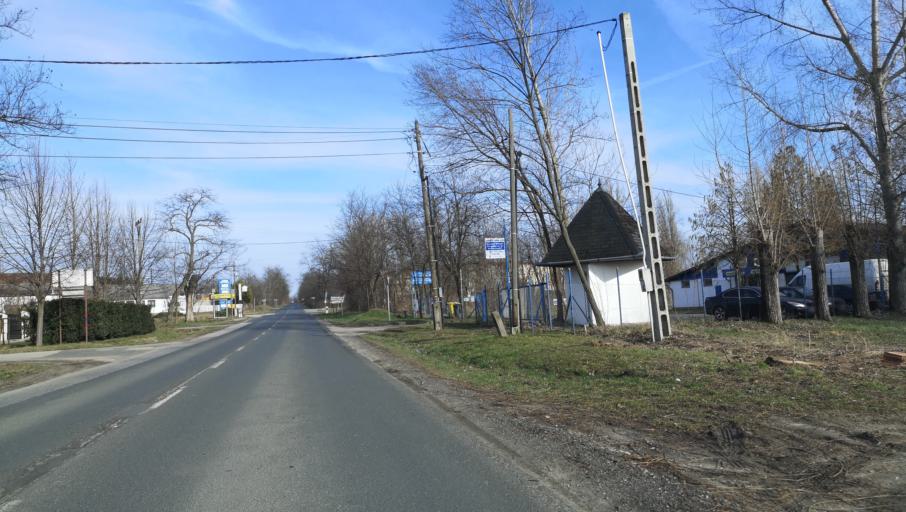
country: HU
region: Pest
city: Monor
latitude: 47.3529
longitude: 19.4627
